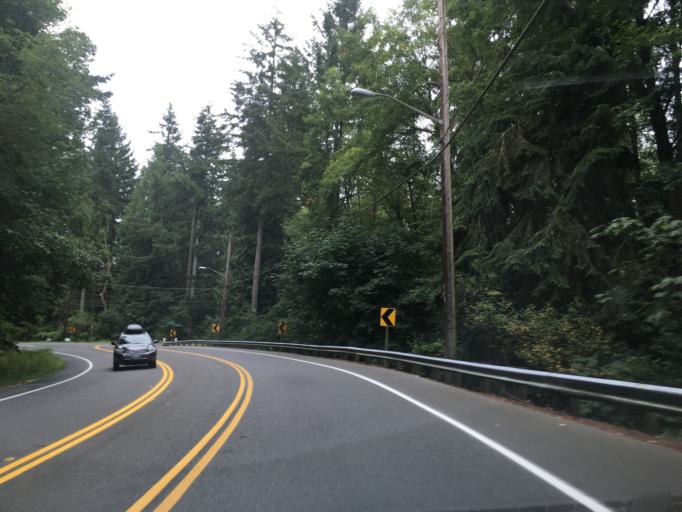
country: US
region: Washington
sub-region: King County
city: Inglewood-Finn Hill
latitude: 47.7258
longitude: -122.2435
